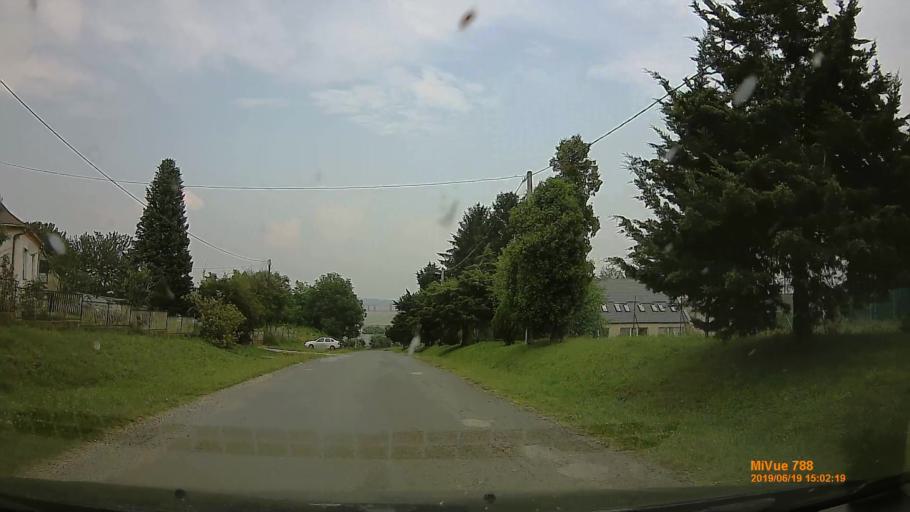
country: HU
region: Baranya
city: Szigetvar
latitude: 46.0904
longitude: 17.8012
